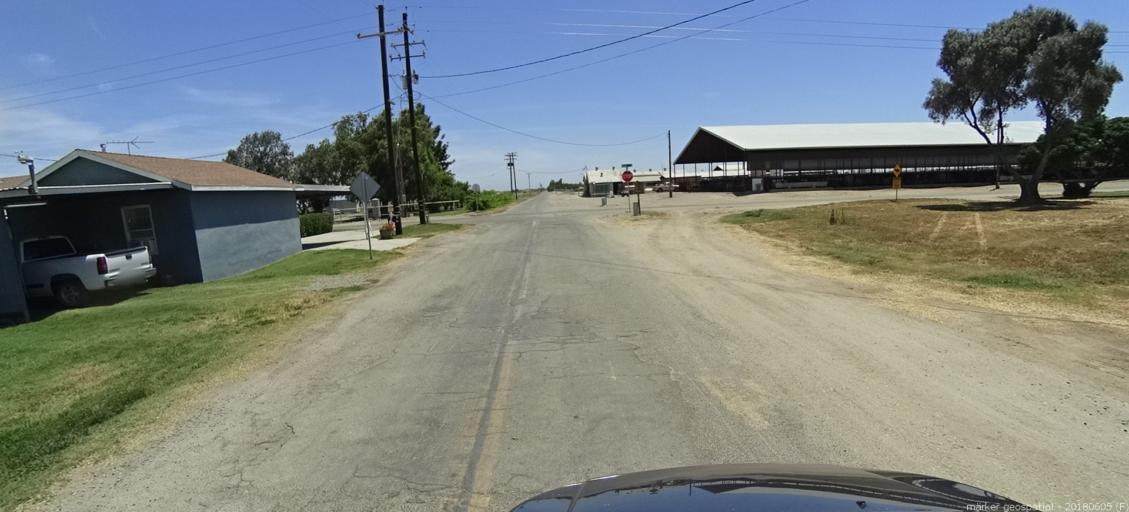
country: US
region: California
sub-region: Madera County
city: Chowchilla
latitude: 37.0906
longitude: -120.3295
